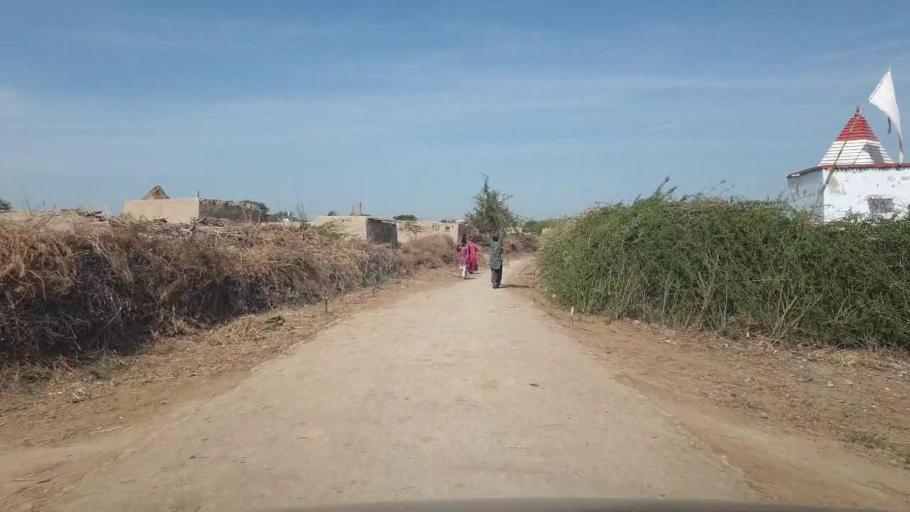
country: PK
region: Sindh
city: Kunri
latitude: 25.3249
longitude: 69.5802
